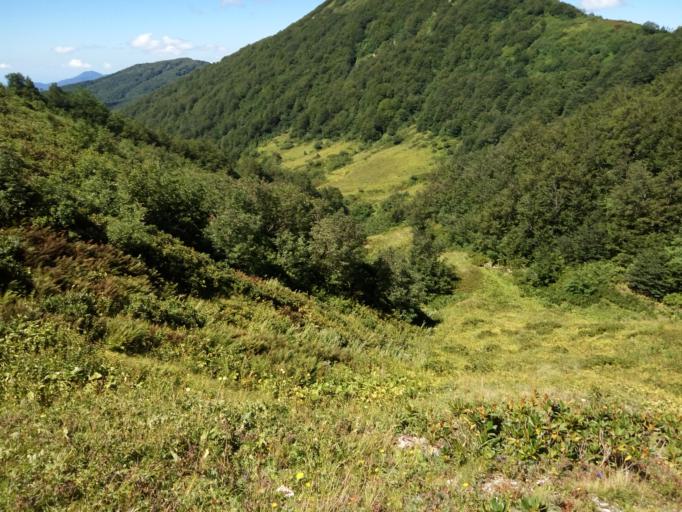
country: RU
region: Krasnodarskiy
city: Dagomys
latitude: 43.9331
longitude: 39.8877
